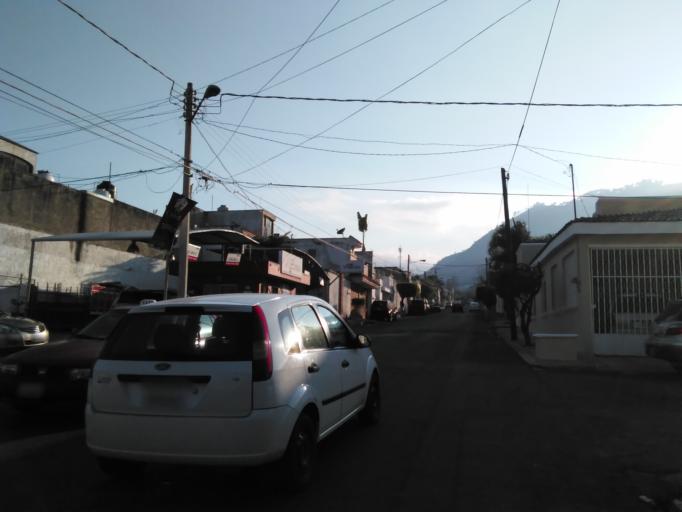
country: MX
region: Nayarit
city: Tepic
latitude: 21.5046
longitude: -104.9116
